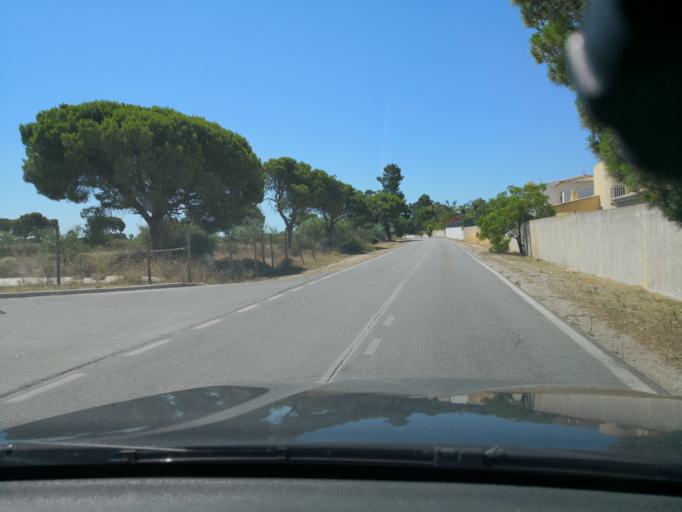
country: PT
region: Faro
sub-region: Loule
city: Vilamoura
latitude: 37.0851
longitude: -8.1008
